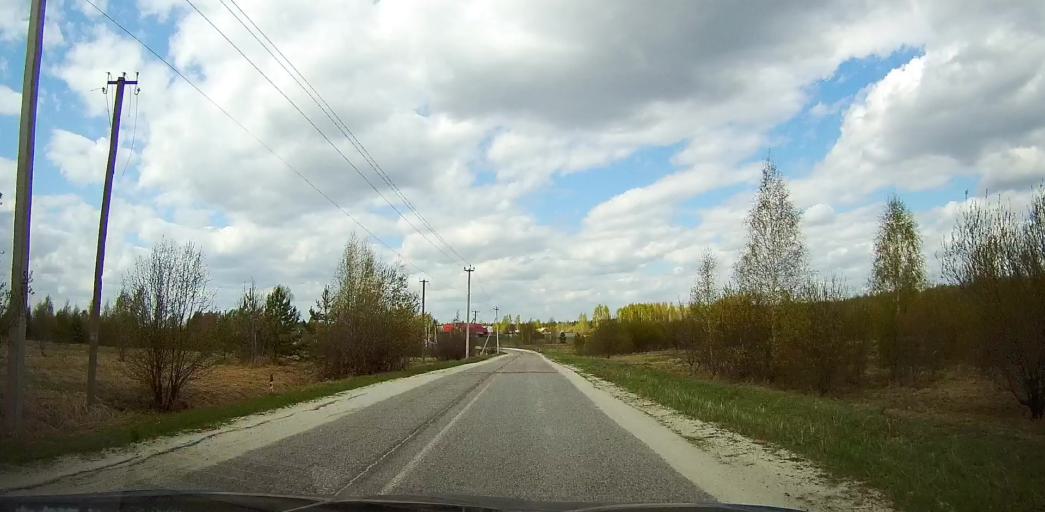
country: RU
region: Moskovskaya
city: Davydovo
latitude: 55.6342
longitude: 38.7830
